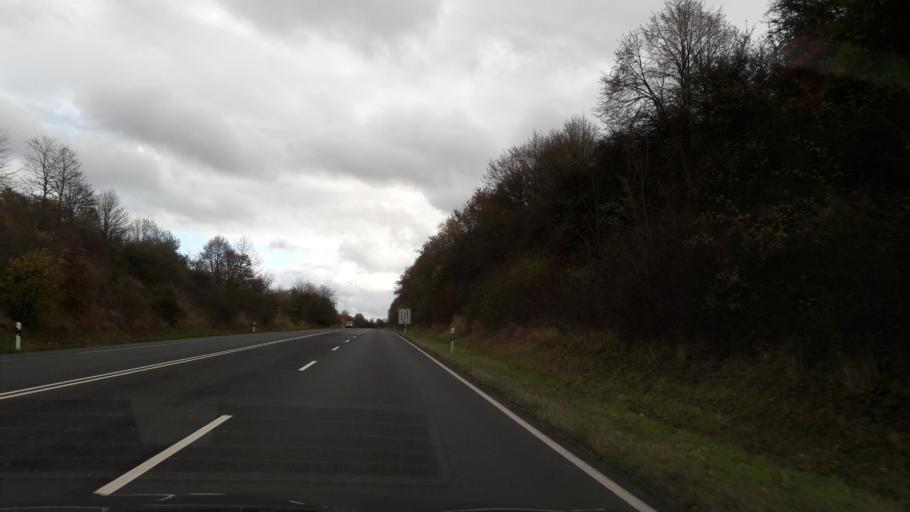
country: DE
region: Rheinland-Pfalz
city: Waldrach
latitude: 49.7657
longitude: 6.7593
